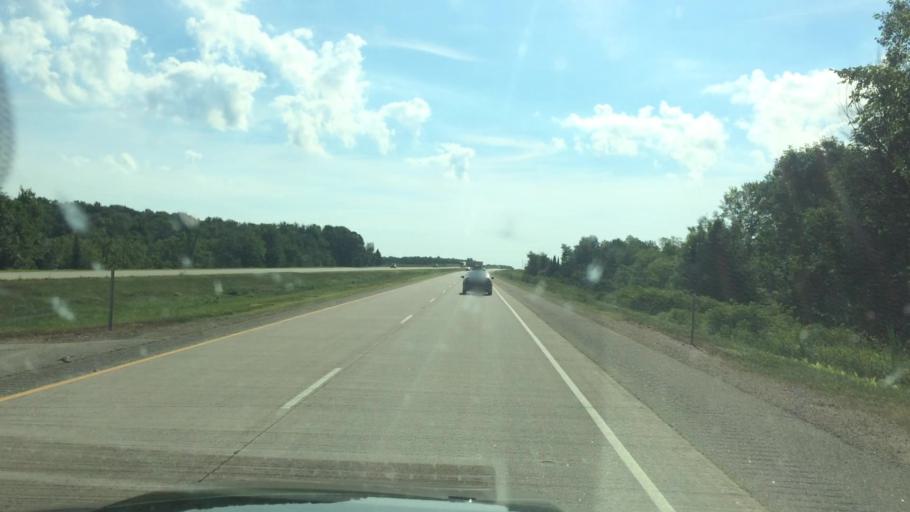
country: US
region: Wisconsin
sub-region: Shawano County
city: Wittenberg
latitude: 44.8036
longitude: -89.0116
